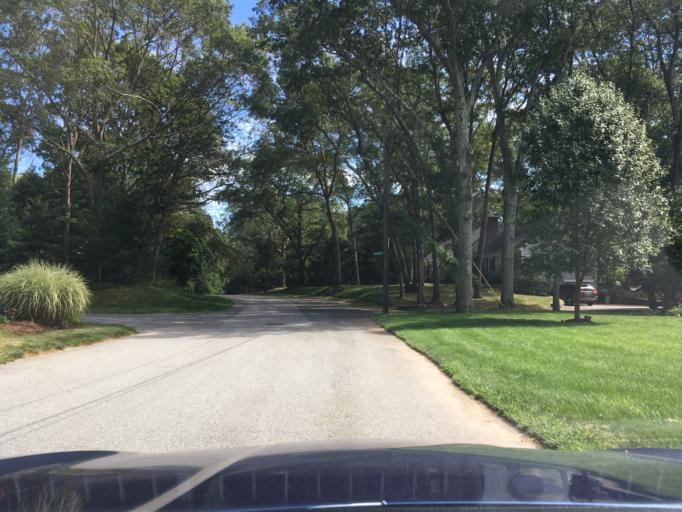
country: US
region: Rhode Island
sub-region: Kent County
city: East Greenwich
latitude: 41.6579
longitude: -71.4713
